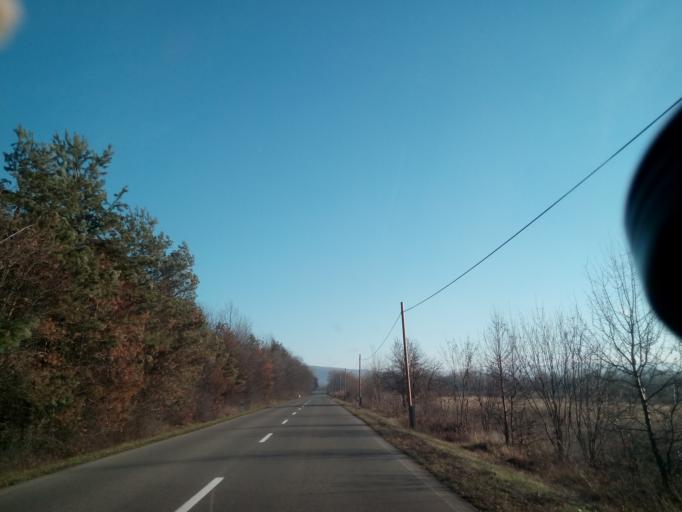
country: SK
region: Kosicky
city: Sobrance
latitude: 48.8217
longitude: 22.1110
